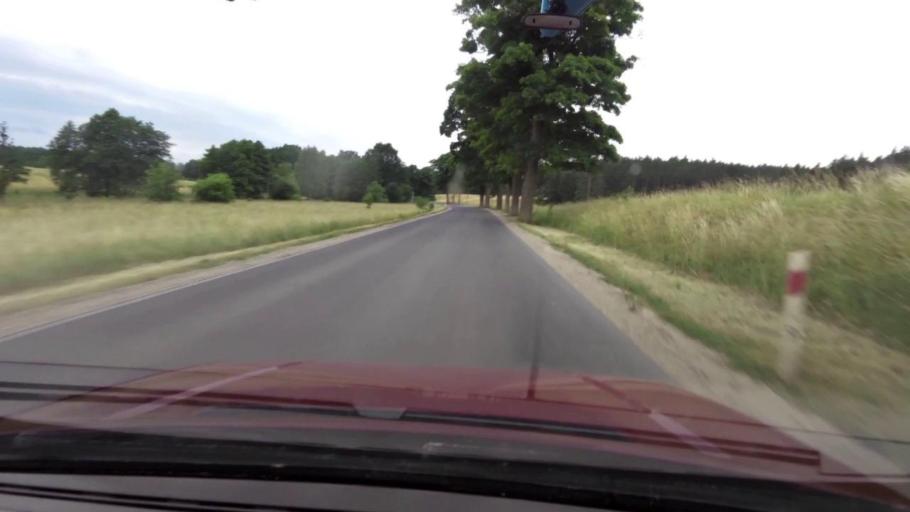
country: PL
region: West Pomeranian Voivodeship
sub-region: Powiat koszalinski
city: Sianow
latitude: 54.1687
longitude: 16.4289
